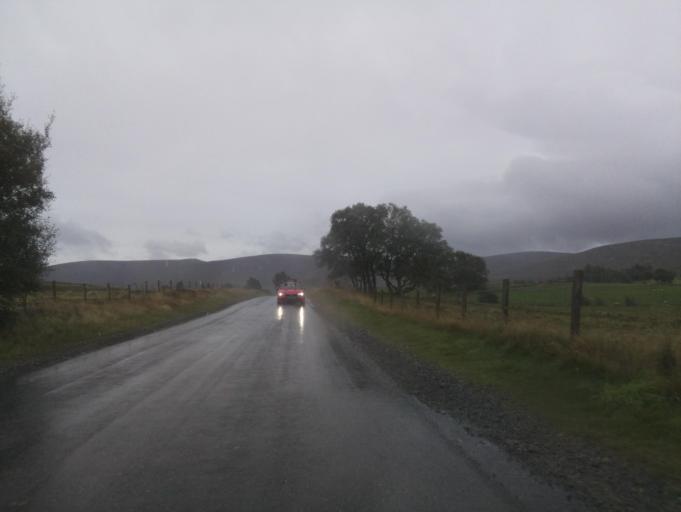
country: GB
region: Scotland
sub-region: Highland
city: Grantown on Spey
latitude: 57.3008
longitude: -3.5571
